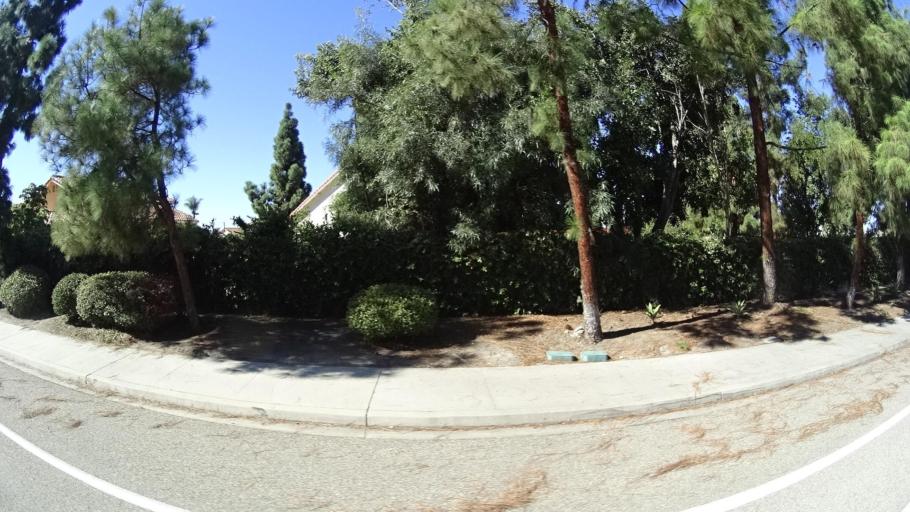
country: US
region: California
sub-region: San Diego County
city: Bonita
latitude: 32.6553
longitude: -116.9906
